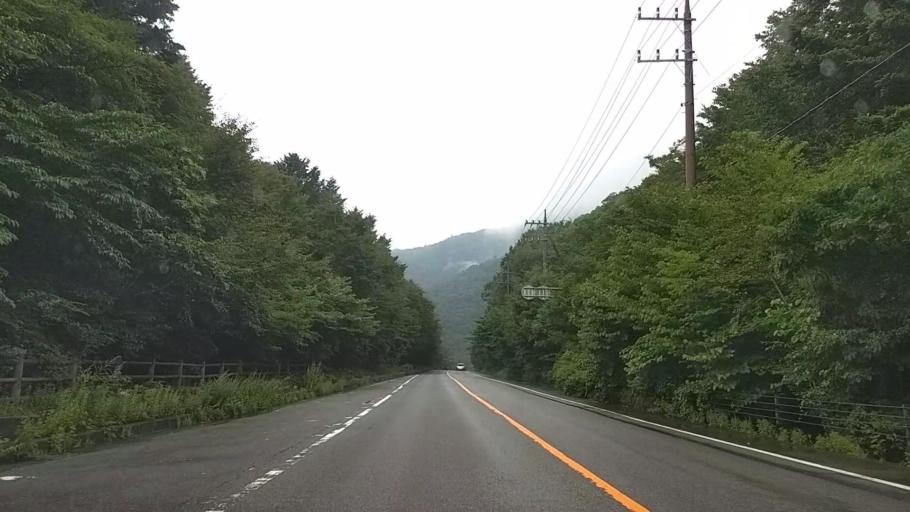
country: JP
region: Yamanashi
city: Fujikawaguchiko
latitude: 35.4871
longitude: 138.6292
